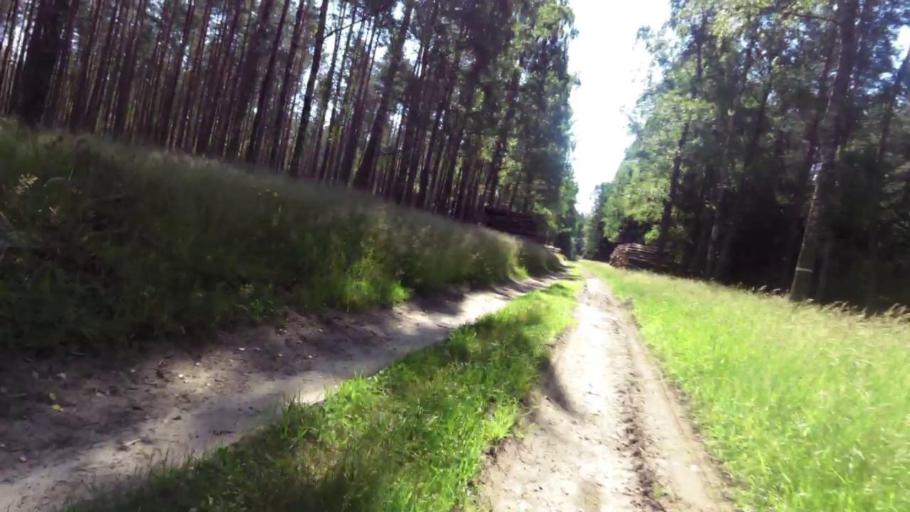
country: PL
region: West Pomeranian Voivodeship
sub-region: Powiat swidwinski
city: Polczyn-Zdroj
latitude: 53.8782
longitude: 16.0998
